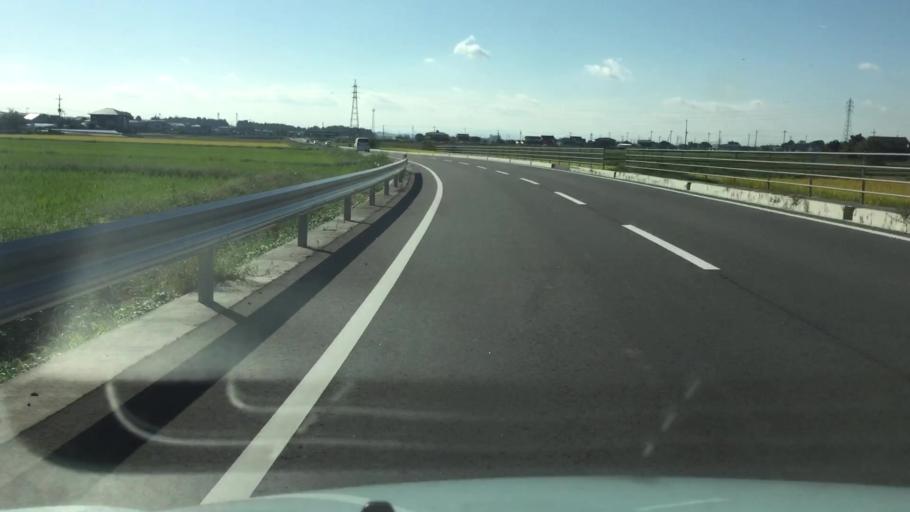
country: JP
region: Tochigi
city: Ujiie
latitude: 36.6606
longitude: 140.0192
